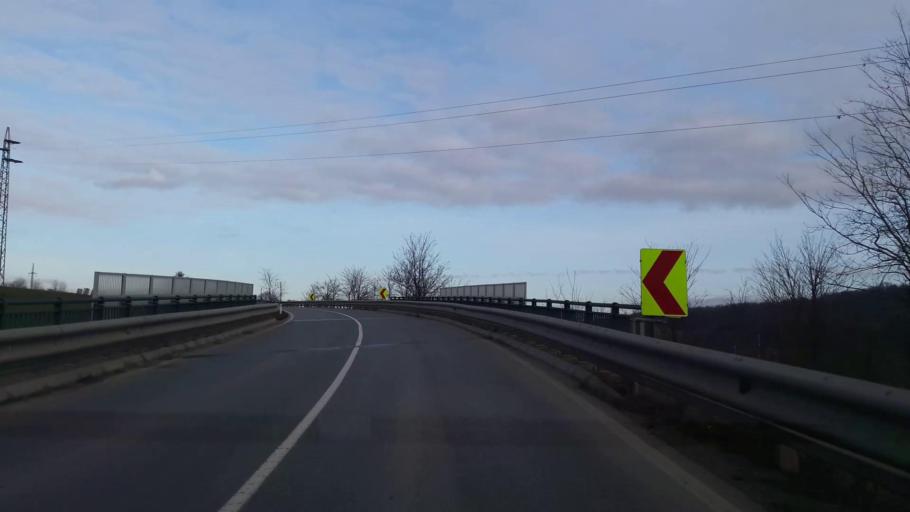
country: AT
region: Lower Austria
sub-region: Politischer Bezirk Mistelbach
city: Staatz
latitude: 48.6337
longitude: 16.5190
